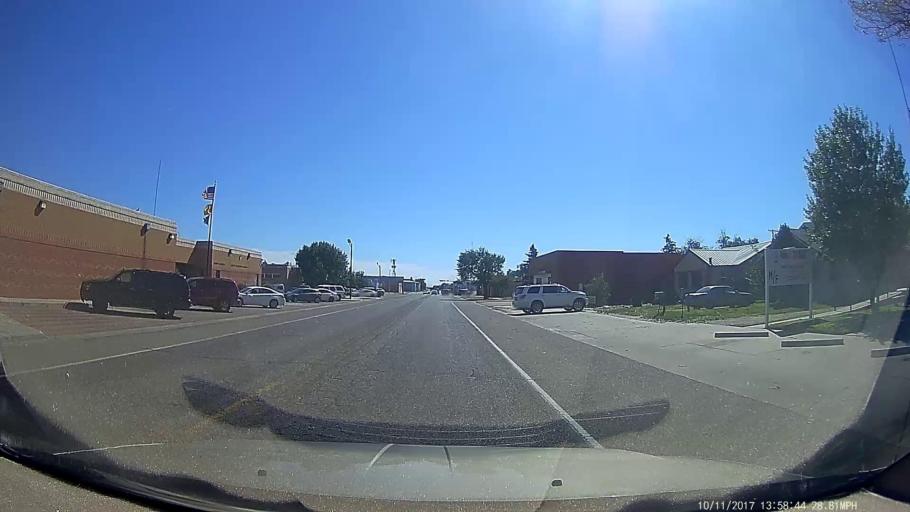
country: US
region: New Mexico
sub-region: Curry County
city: Clovis
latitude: 34.4065
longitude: -103.2067
